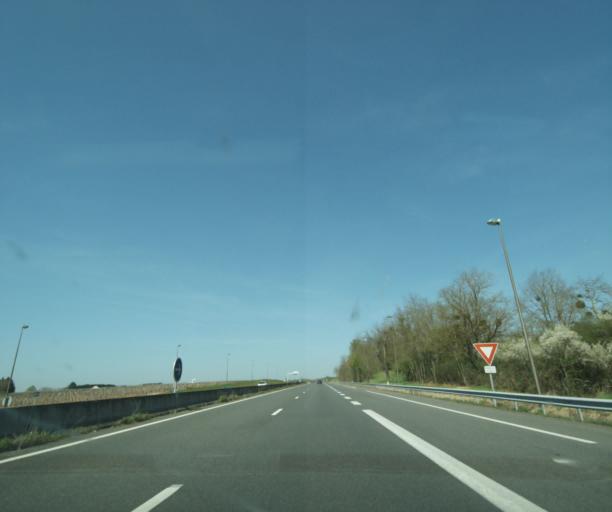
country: FR
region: Bourgogne
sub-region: Departement de la Nievre
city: Pouilly-sur-Loire
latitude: 47.2745
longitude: 2.9765
